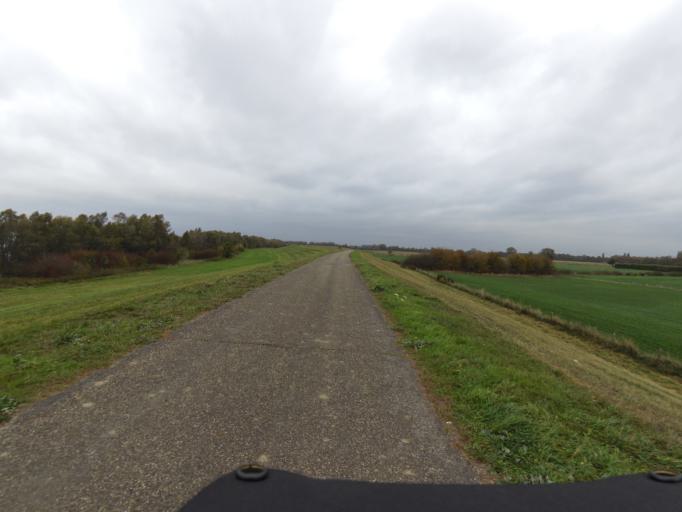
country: NL
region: Gelderland
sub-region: Gemeente Zevenaar
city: Zevenaar
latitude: 51.8643
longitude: 6.1000
